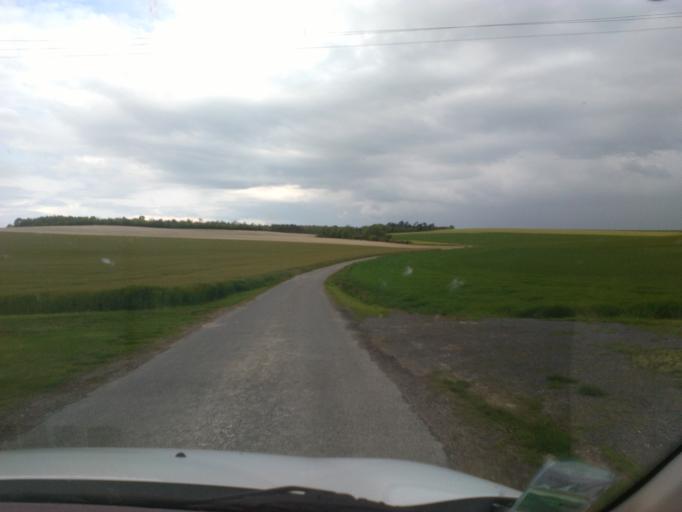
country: FR
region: Bourgogne
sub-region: Departement de l'Yonne
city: Thorigny-sur-Oreuse
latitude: 48.3653
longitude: 3.4586
